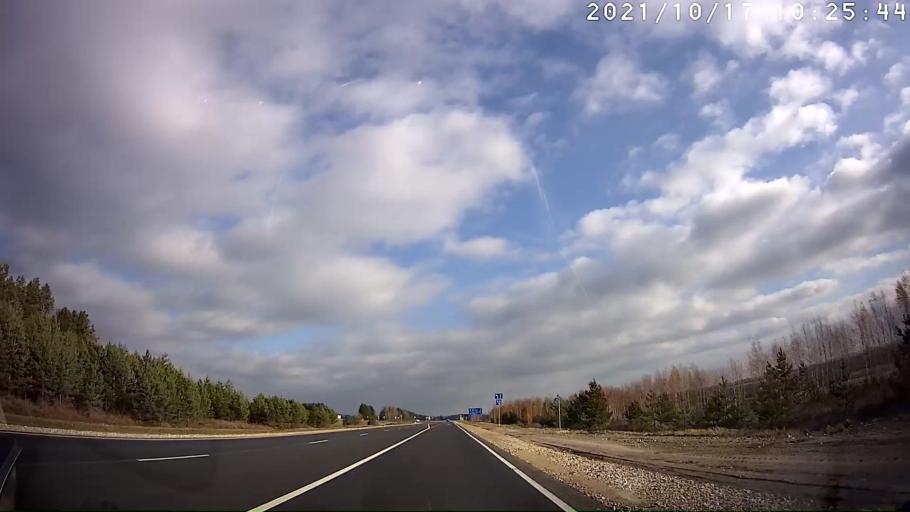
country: RU
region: Mariy-El
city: Kuzhener
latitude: 56.8152
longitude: 48.7100
